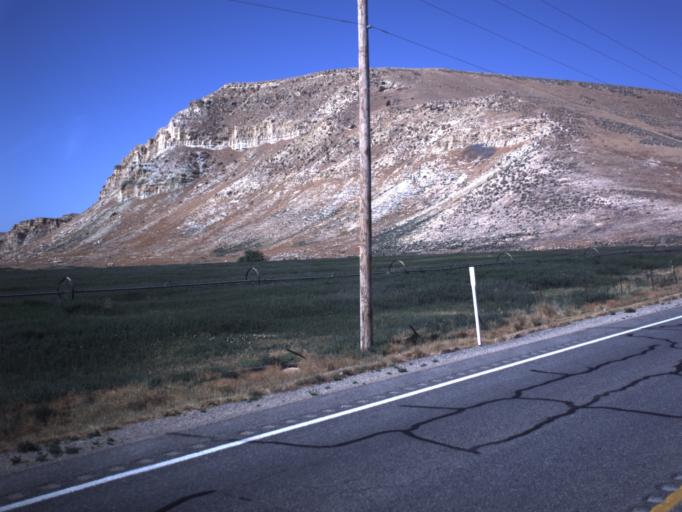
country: US
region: Utah
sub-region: Sanpete County
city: Gunnison
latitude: 39.1550
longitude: -111.7690
